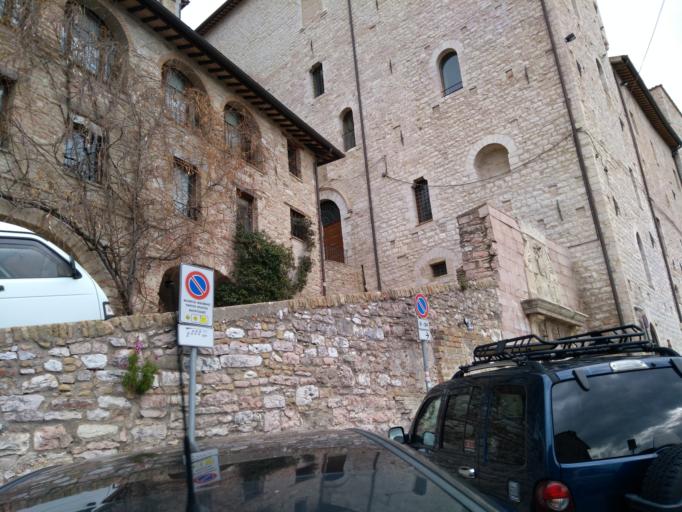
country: IT
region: Umbria
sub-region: Provincia di Perugia
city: Assisi
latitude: 43.0722
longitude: 12.6104
